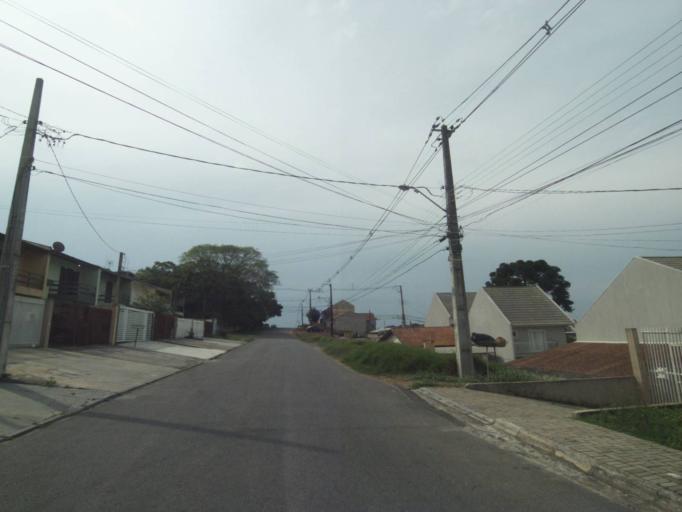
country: BR
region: Parana
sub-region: Pinhais
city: Pinhais
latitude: -25.4176
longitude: -49.2052
